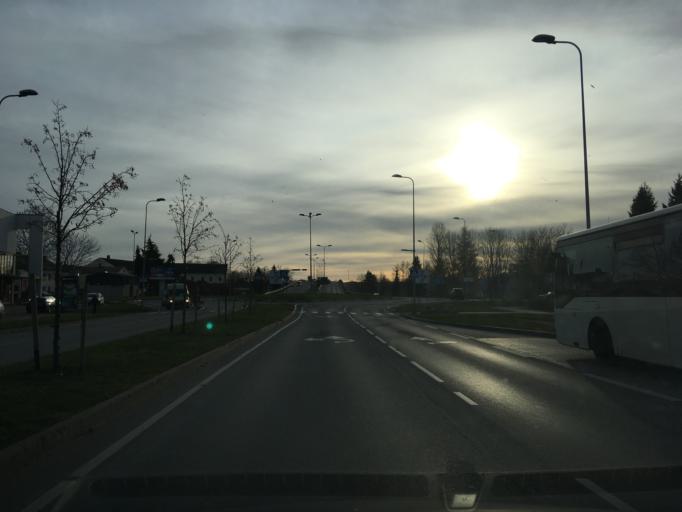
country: EE
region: Ida-Virumaa
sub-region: Johvi vald
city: Johvi
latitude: 59.3583
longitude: 27.4097
